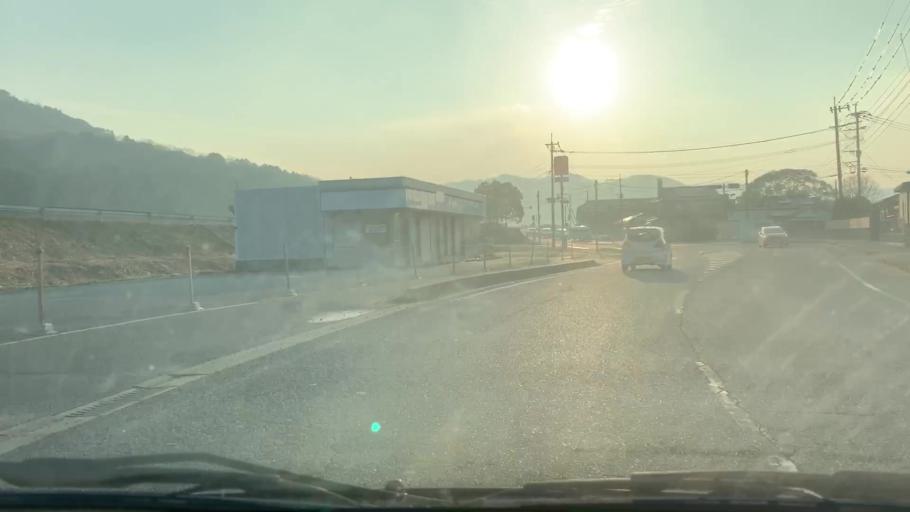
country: JP
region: Saga Prefecture
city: Takeocho-takeo
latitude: 33.2763
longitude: 130.1471
